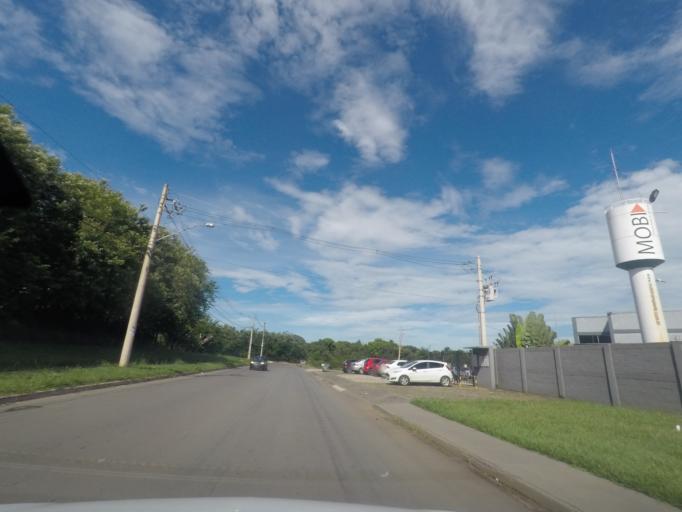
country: BR
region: Goias
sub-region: Aparecida De Goiania
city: Aparecida de Goiania
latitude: -16.7922
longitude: -49.2617
